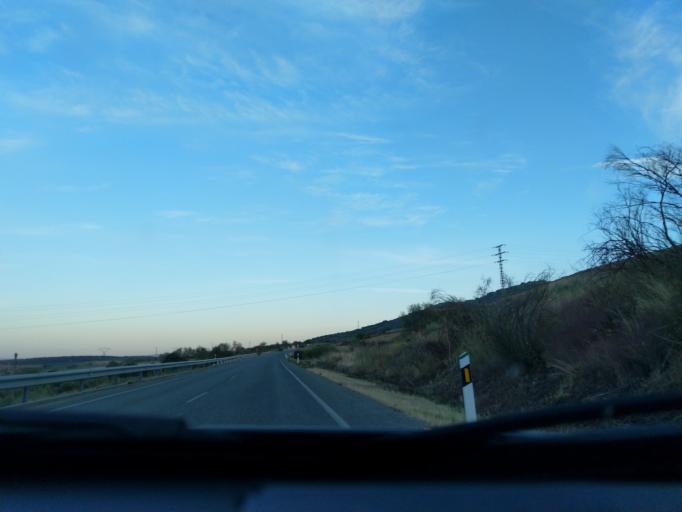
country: ES
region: Extremadura
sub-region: Provincia de Badajoz
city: Reina
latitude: 38.1918
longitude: -5.9490
